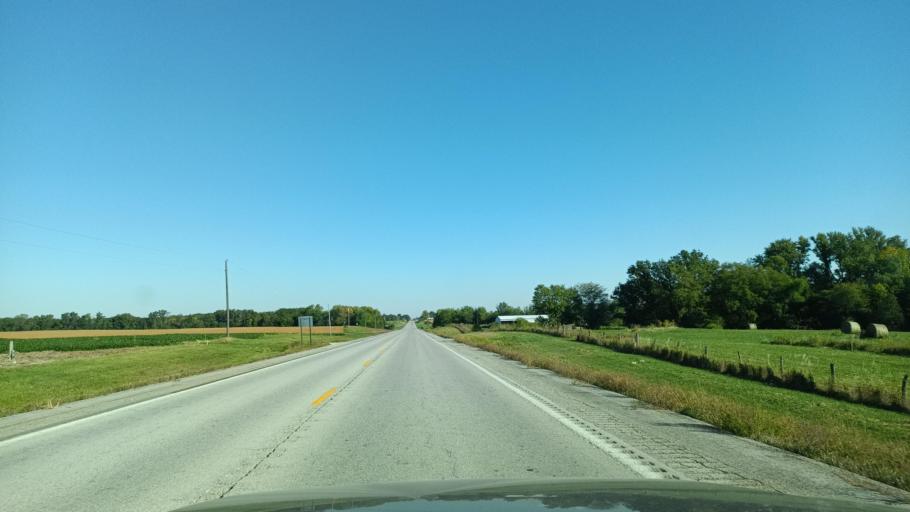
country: US
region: Missouri
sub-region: Audrain County
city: Vandalia
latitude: 39.2982
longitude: -91.6438
